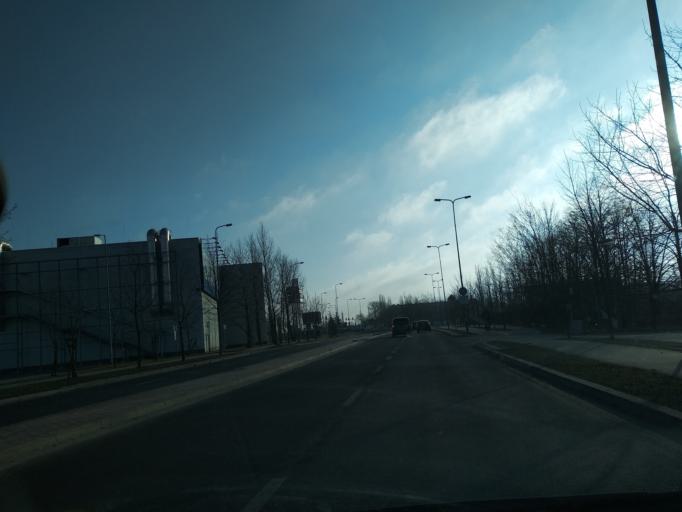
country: PL
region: Masovian Voivodeship
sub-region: Powiat piaseczynski
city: Piaseczno
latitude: 52.0878
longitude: 21.0156
